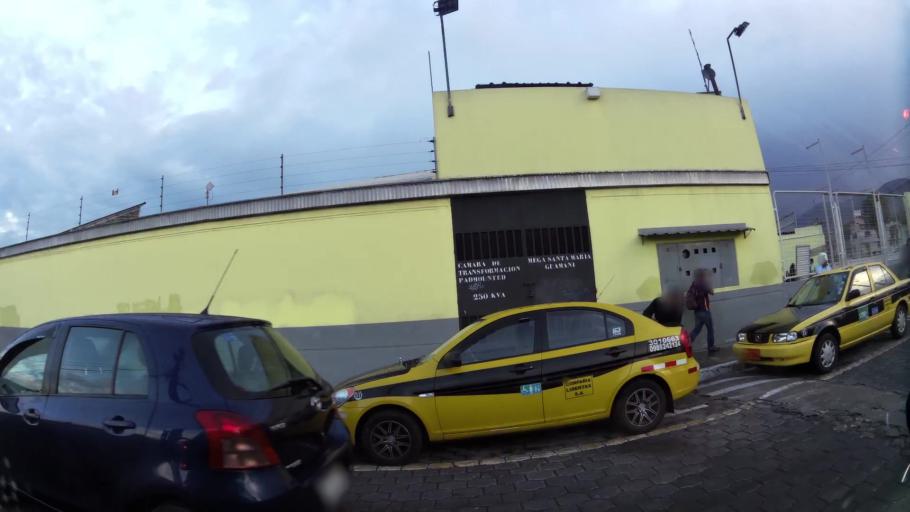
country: EC
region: Pichincha
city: Quito
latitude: -0.3079
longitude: -78.5440
